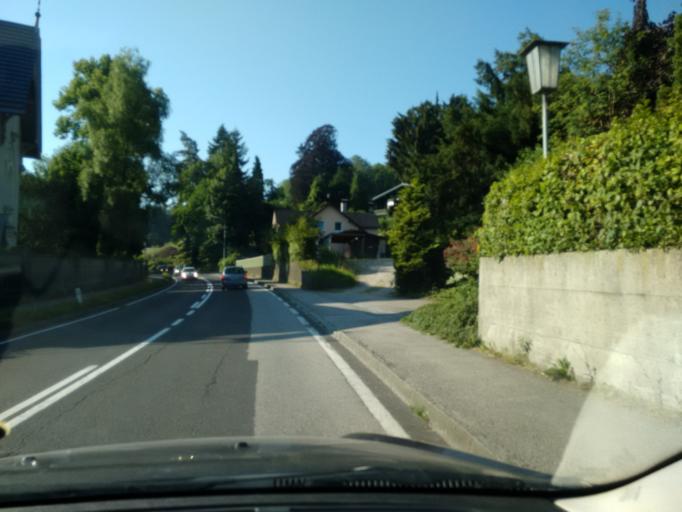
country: AT
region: Upper Austria
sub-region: Politischer Bezirk Gmunden
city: Altmunster
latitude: 47.8915
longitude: 13.7671
